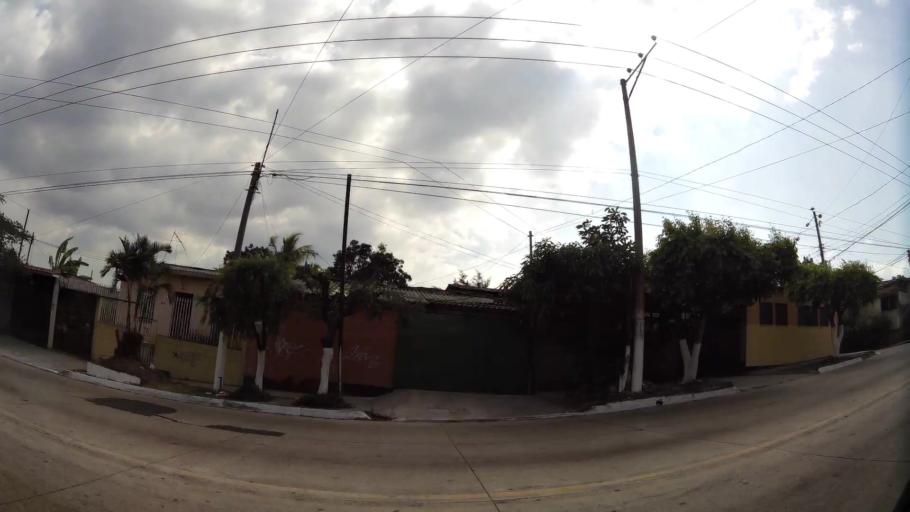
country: SV
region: San Salvador
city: Mejicanos
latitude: 13.7347
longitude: -89.2134
